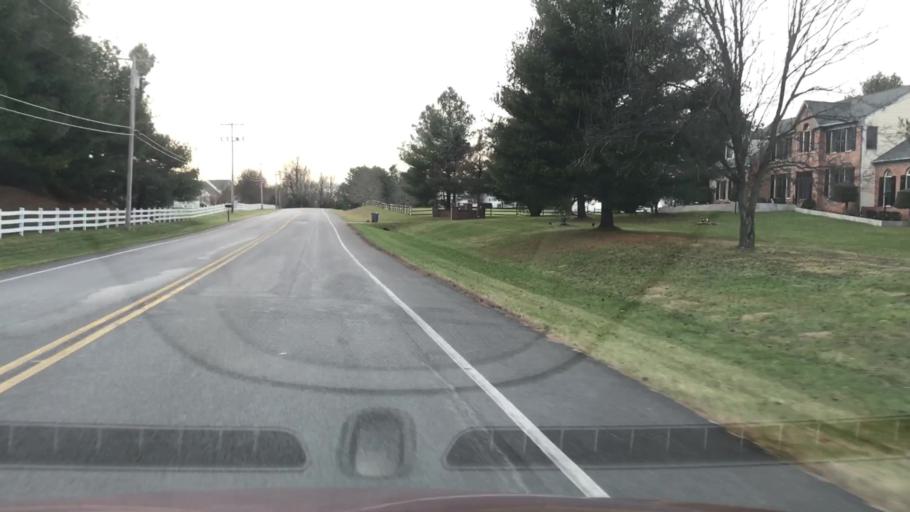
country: US
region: Maryland
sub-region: Howard County
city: Fulton
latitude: 39.1760
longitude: -76.9303
